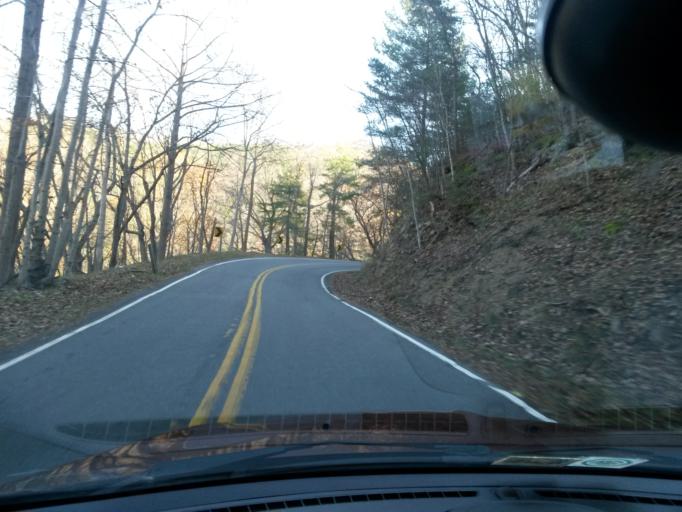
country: US
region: Virginia
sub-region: Botetourt County
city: Buchanan
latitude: 37.4974
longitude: -79.6619
